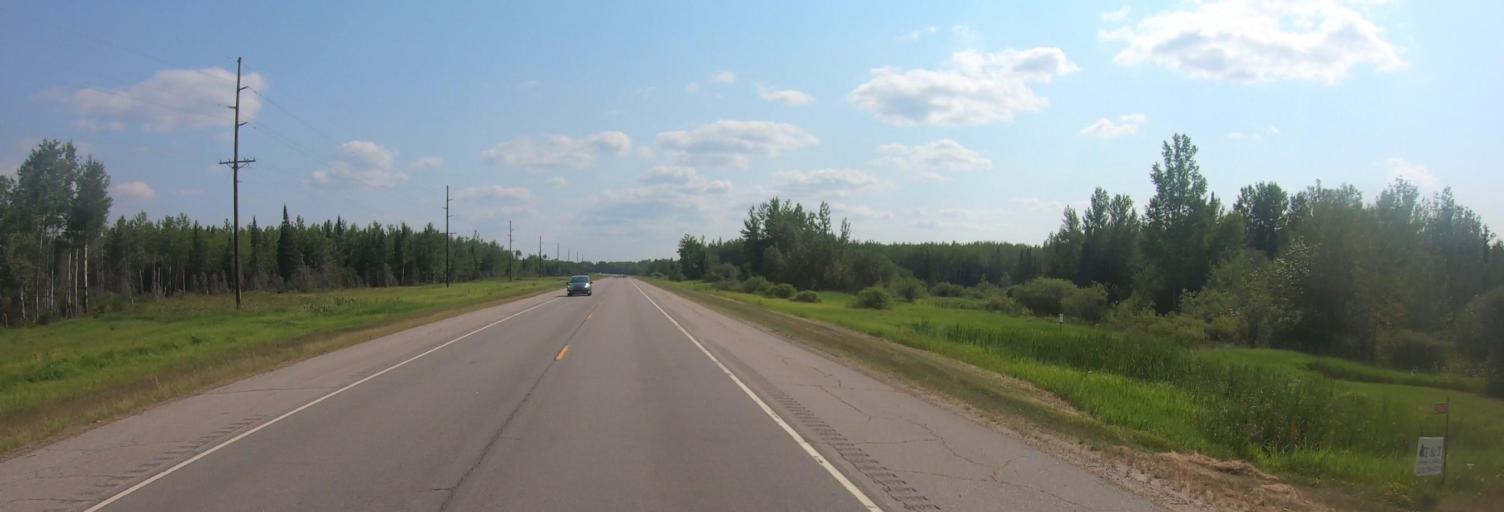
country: US
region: Minnesota
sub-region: Saint Louis County
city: Chisholm
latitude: 47.9402
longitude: -92.8307
